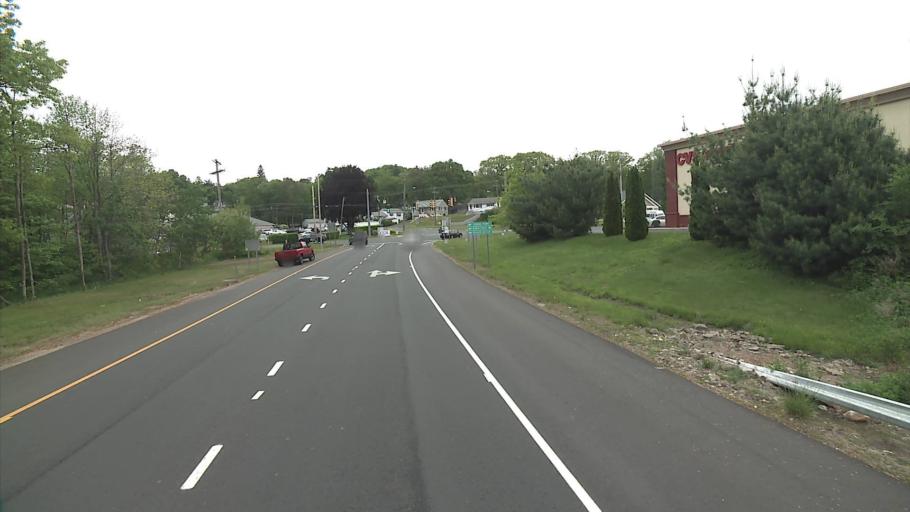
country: US
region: Connecticut
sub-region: New Haven County
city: Waterbury
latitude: 41.5511
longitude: -73.0642
